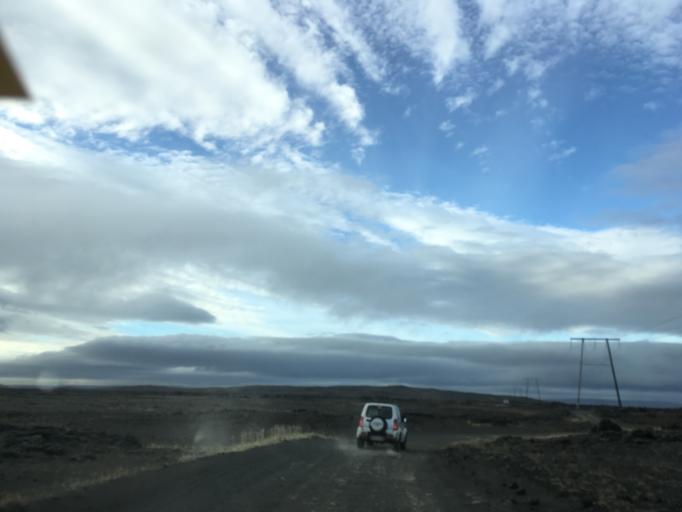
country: IS
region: South
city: Vestmannaeyjar
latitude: 64.1371
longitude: -19.1272
